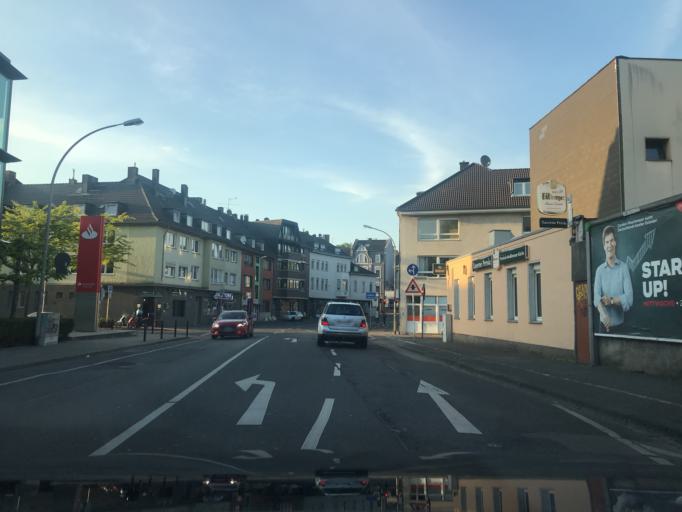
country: DE
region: North Rhine-Westphalia
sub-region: Regierungsbezirk Dusseldorf
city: Monchengladbach
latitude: 51.1947
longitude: 6.4254
